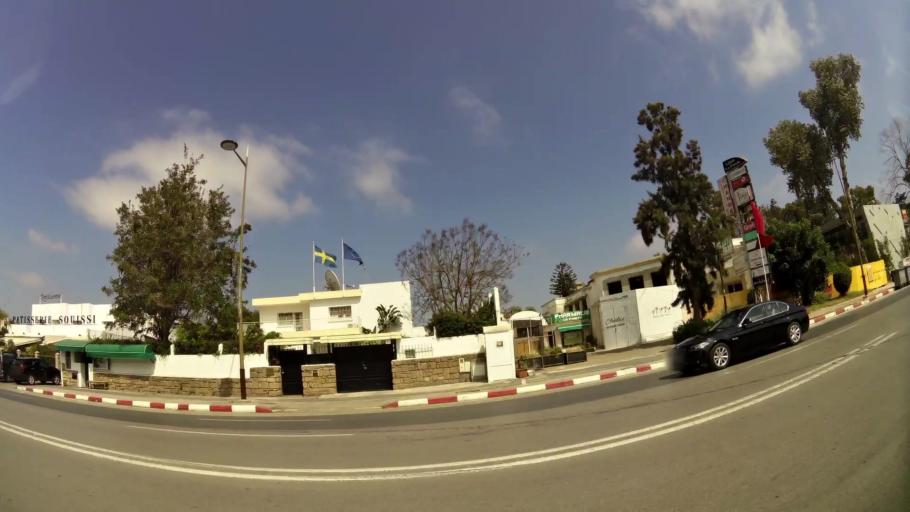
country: MA
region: Rabat-Sale-Zemmour-Zaer
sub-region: Rabat
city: Rabat
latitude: 33.9854
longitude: -6.8288
